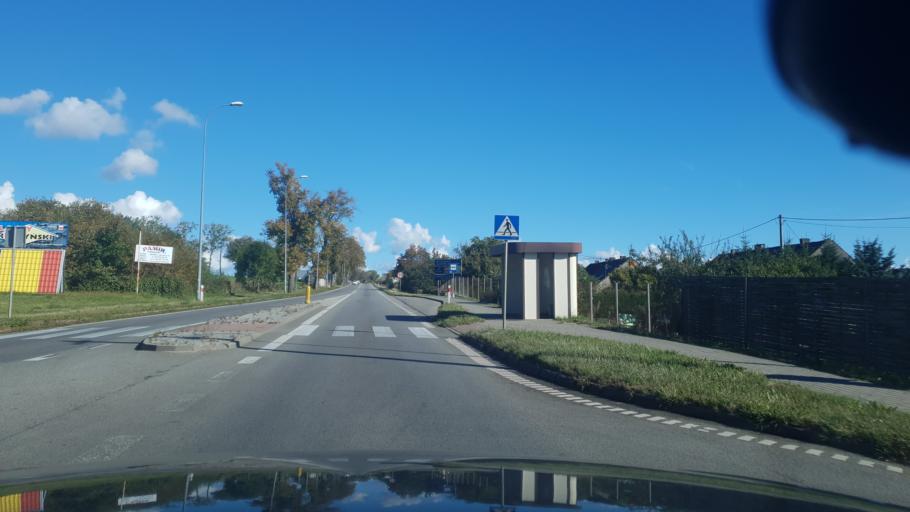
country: PL
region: Pomeranian Voivodeship
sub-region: Powiat wejherowski
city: Rekowo Dolne
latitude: 54.6624
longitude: 18.3632
